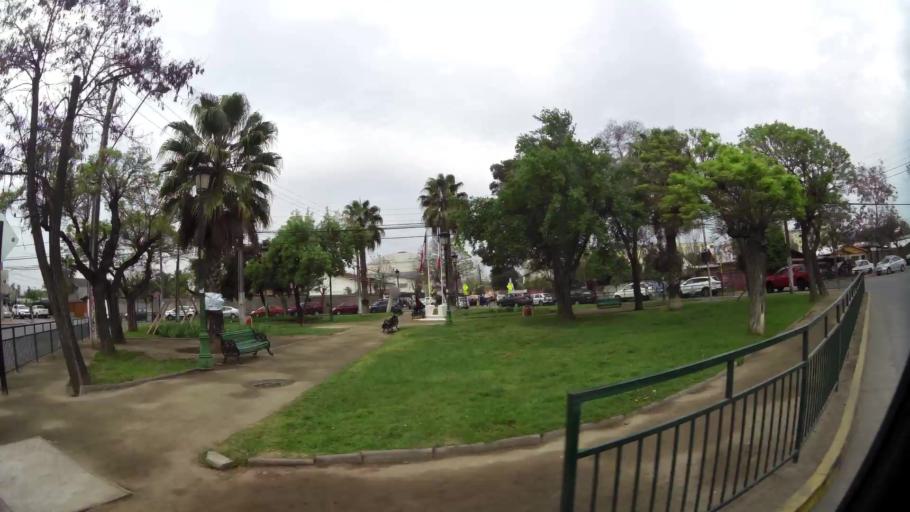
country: CL
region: Santiago Metropolitan
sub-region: Provincia de Santiago
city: Lo Prado
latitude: -33.5015
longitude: -70.7644
